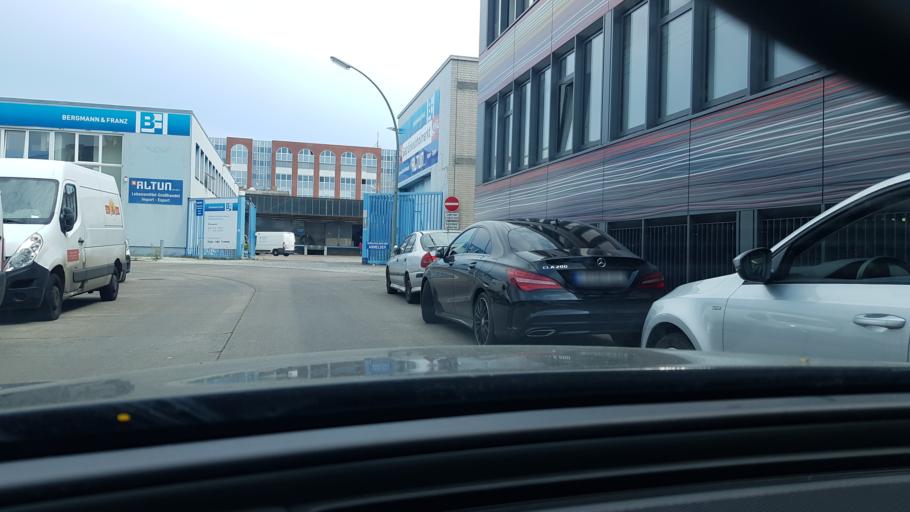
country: DE
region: Berlin
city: Charlottenburg-Nord
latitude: 52.5446
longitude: 13.3140
